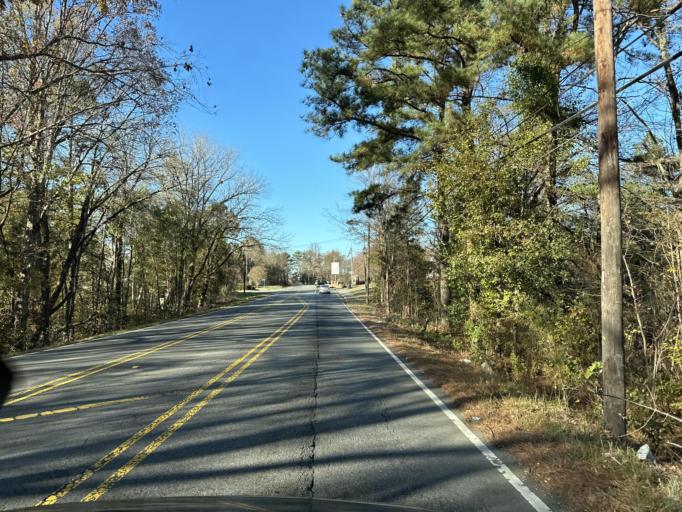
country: US
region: North Carolina
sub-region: Gaston County
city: Mount Holly
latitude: 35.3076
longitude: -80.9386
